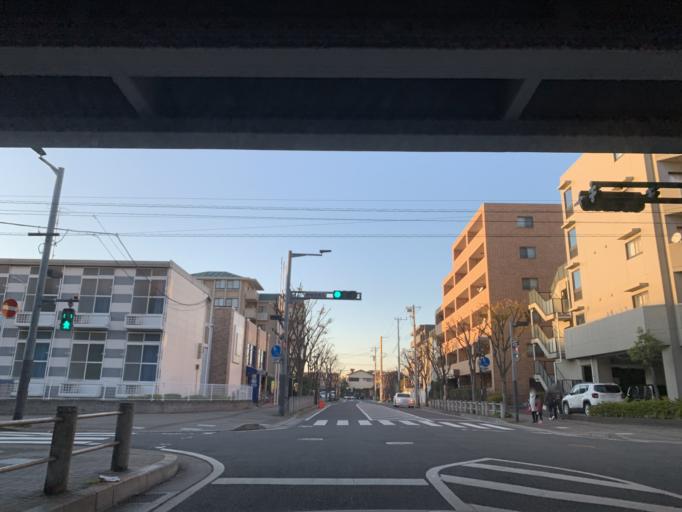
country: JP
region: Tokyo
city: Urayasu
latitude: 35.6930
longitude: 139.9267
